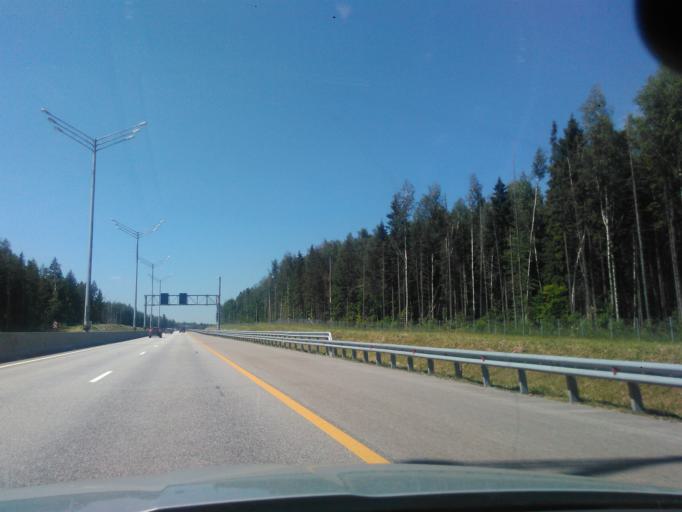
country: RU
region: Moskovskaya
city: Mendeleyevo
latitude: 56.0656
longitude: 37.2313
